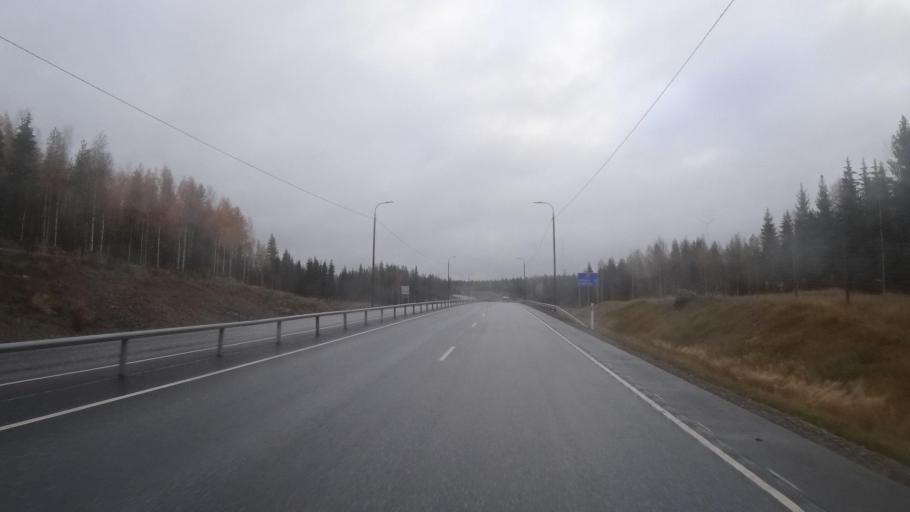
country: FI
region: Northern Savo
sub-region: Varkaus
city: Varkaus
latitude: 62.3393
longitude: 28.0427
